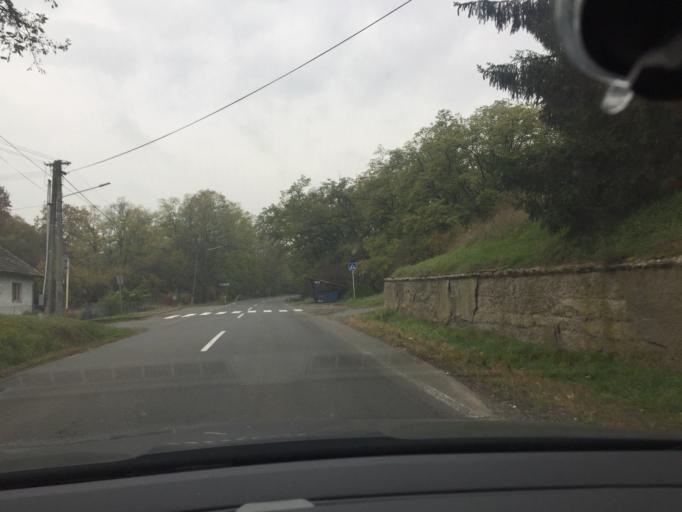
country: SK
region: Banskobystricky
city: Velky Krtis
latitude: 48.2664
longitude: 19.4453
